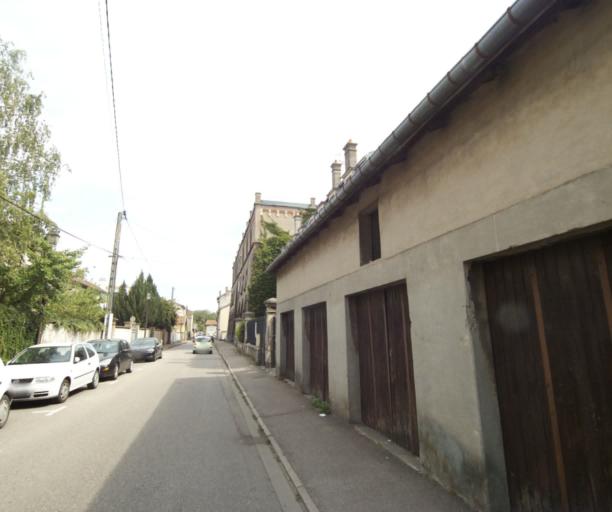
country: FR
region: Lorraine
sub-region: Departement de Meurthe-et-Moselle
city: Luneville
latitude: 48.5914
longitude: 6.5025
